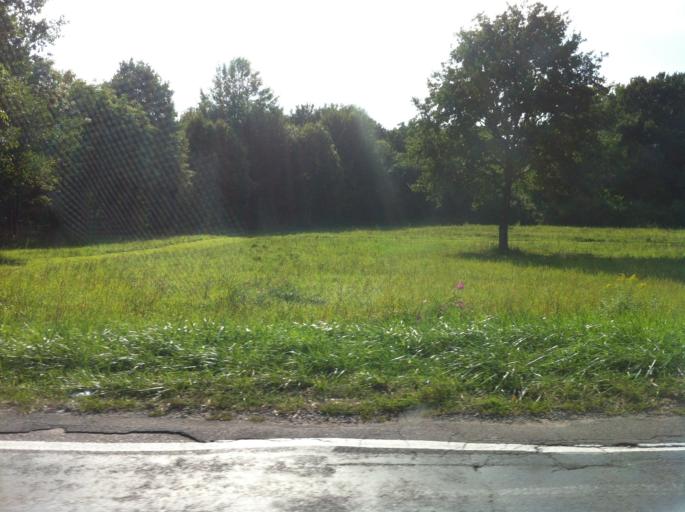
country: DE
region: Saxony
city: Markkleeberg
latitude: 51.2861
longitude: 12.3622
